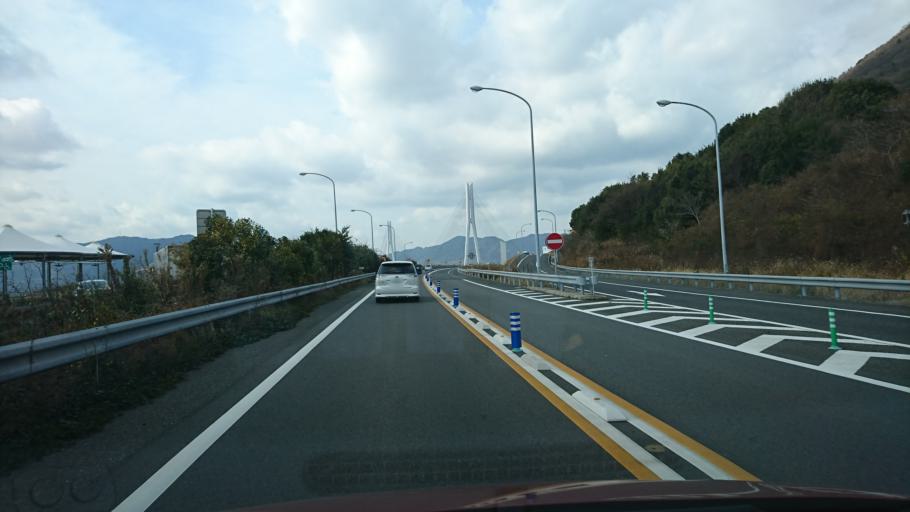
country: JP
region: Hiroshima
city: Innoshima
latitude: 34.2595
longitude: 133.0823
